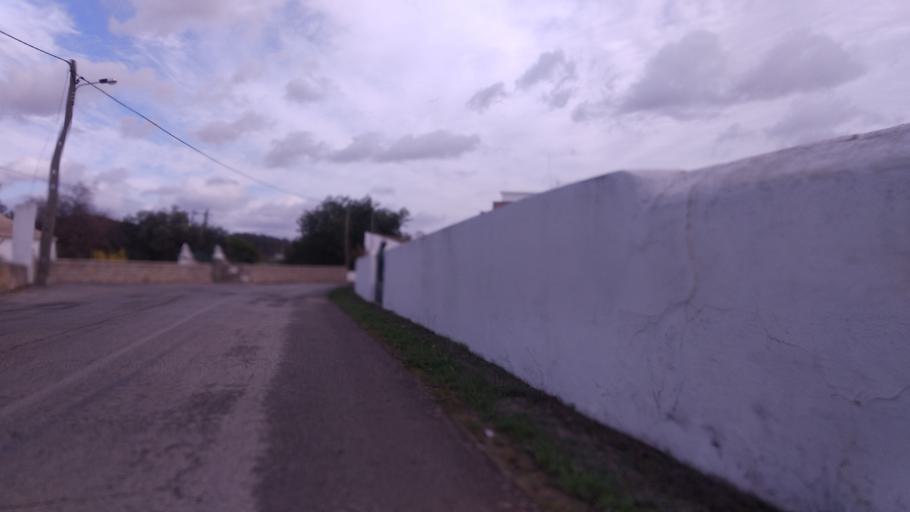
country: PT
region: Faro
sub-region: Sao Bras de Alportel
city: Sao Bras de Alportel
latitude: 37.1704
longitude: -7.8978
